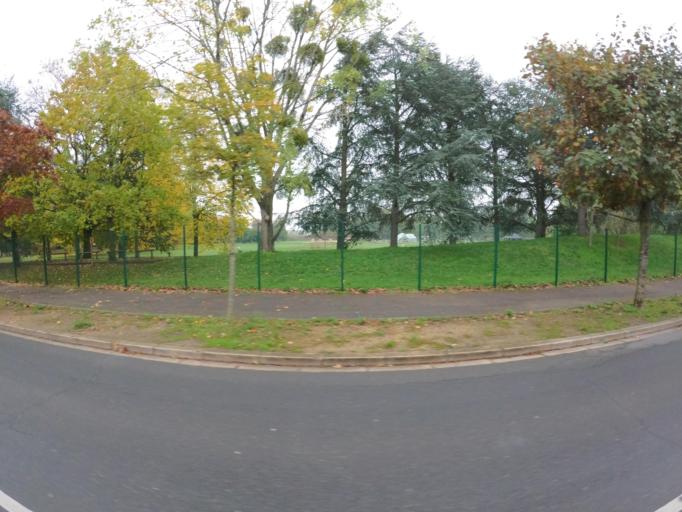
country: FR
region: Ile-de-France
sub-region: Departement du Val-de-Marne
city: Ormesson-sur-Marne
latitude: 48.7973
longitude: 2.5594
